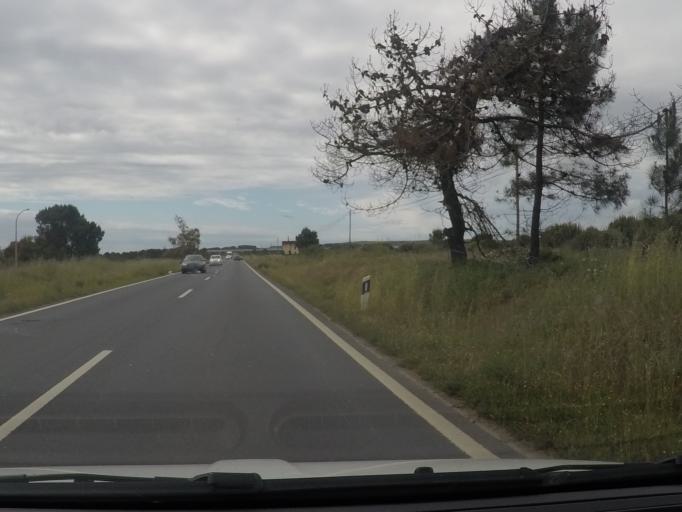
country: PT
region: Setubal
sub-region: Sines
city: Sines
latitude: 37.9314
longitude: -8.8113
